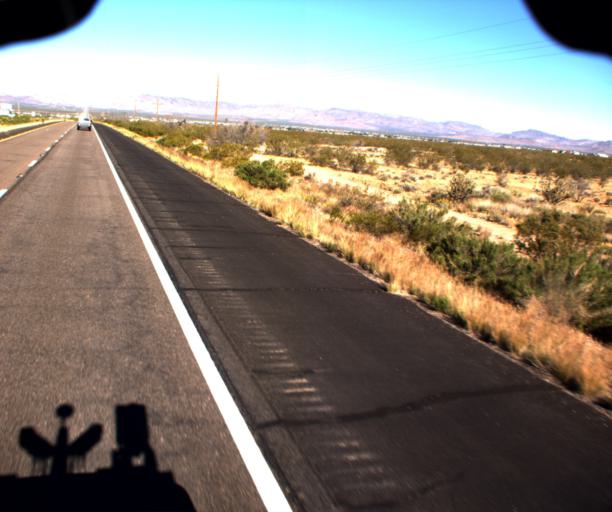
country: US
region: Arizona
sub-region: Mohave County
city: Golden Valley
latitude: 35.2241
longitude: -114.2554
